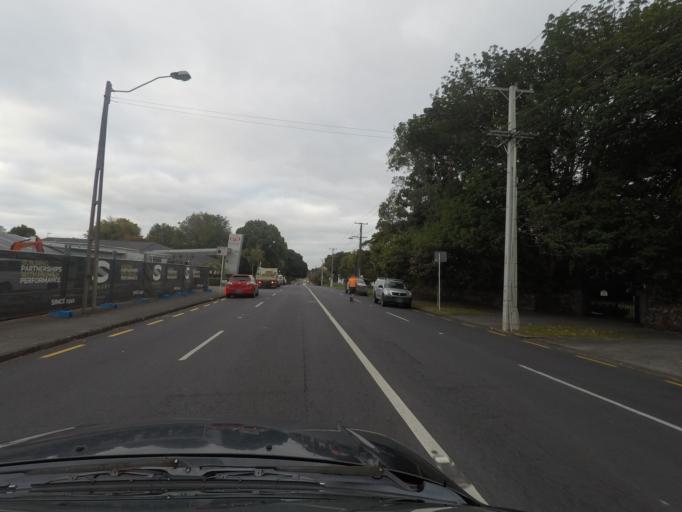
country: NZ
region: Auckland
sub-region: Auckland
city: Auckland
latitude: -36.8806
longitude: 174.7721
